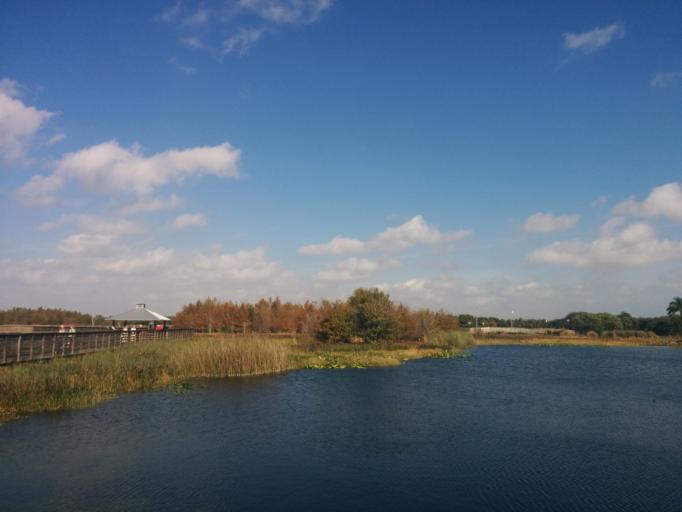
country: US
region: Florida
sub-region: Palm Beach County
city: Villages of Oriole
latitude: 26.4848
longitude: -80.1603
